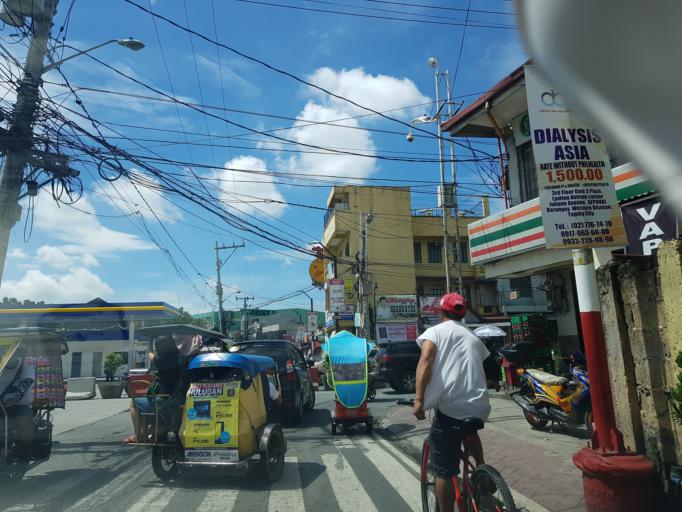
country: PH
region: Calabarzon
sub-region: Province of Rizal
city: Pateros
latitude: 14.5320
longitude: 121.0695
